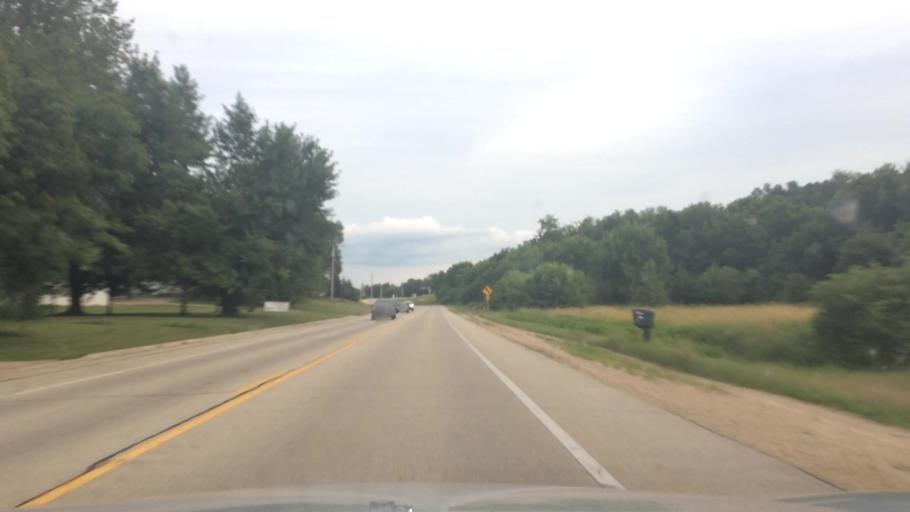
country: US
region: Wisconsin
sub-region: Columbia County
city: Lodi
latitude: 43.2988
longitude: -89.5237
